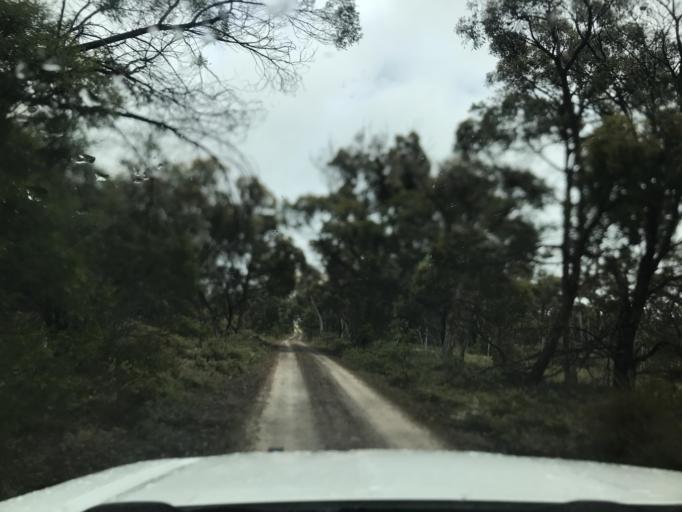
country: AU
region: South Australia
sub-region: Wattle Range
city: Penola
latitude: -37.2639
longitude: 141.3071
